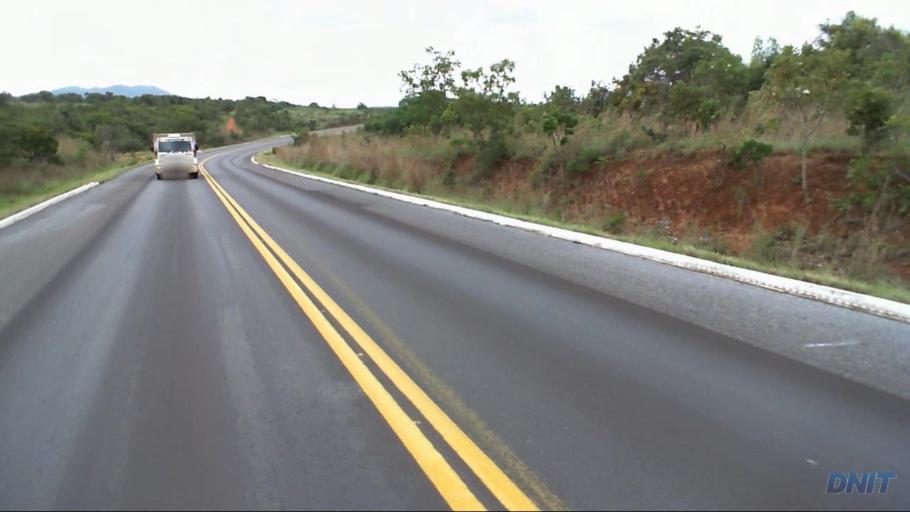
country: BR
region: Goias
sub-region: Padre Bernardo
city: Padre Bernardo
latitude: -15.2201
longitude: -48.6442
